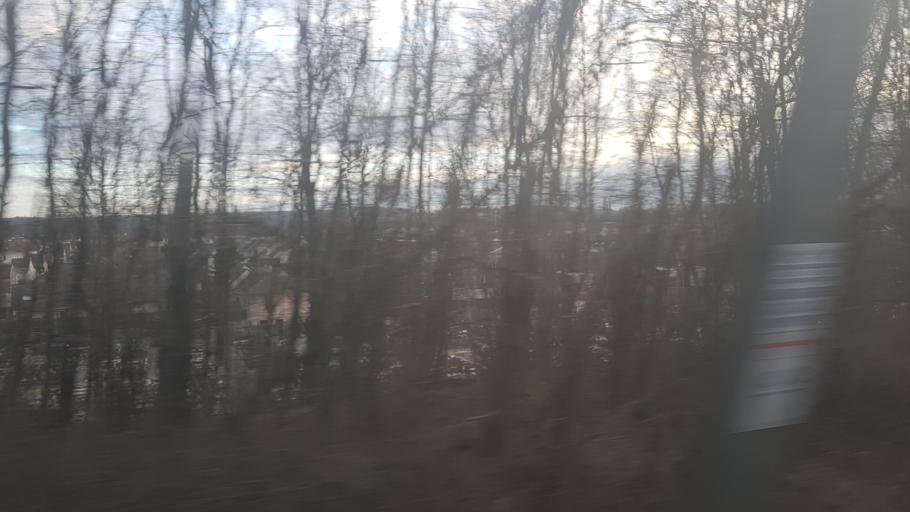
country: FR
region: Lorraine
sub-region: Departement des Vosges
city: Thaon-les-Vosges
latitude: 48.2548
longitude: 6.4084
